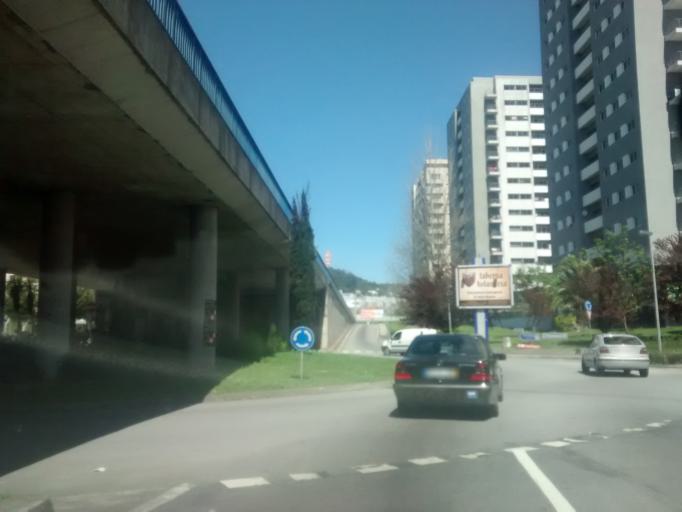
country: PT
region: Braga
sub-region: Braga
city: Braga
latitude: 41.5598
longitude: -8.4073
